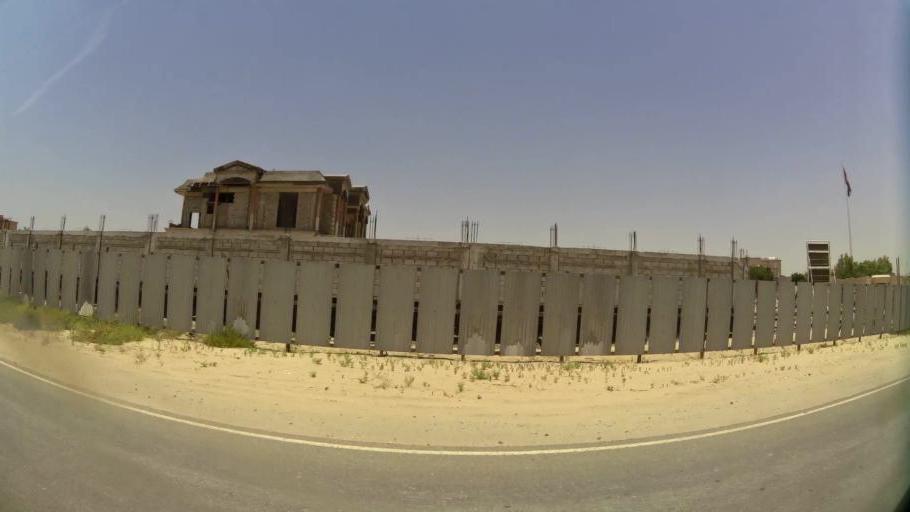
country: AE
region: Ajman
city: Ajman
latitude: 25.4118
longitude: 55.4948
